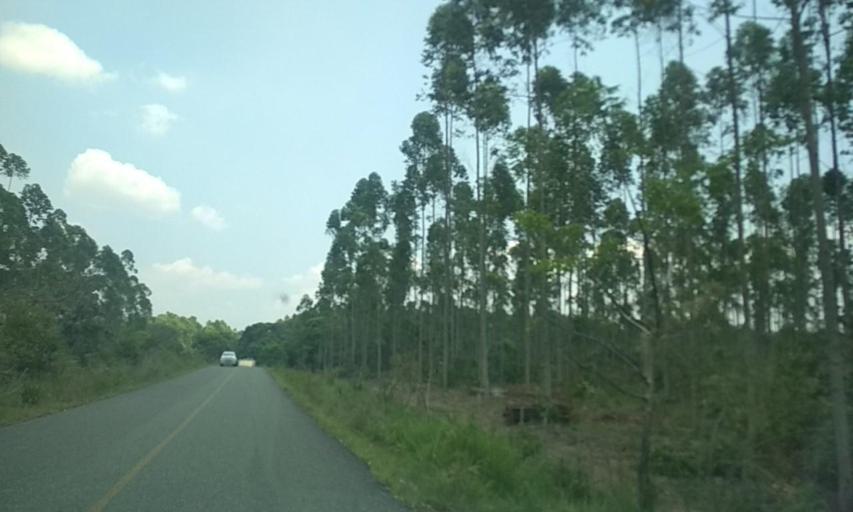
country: MX
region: Tabasco
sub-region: Huimanguillo
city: Francisco Rueda
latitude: 17.8418
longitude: -93.8923
